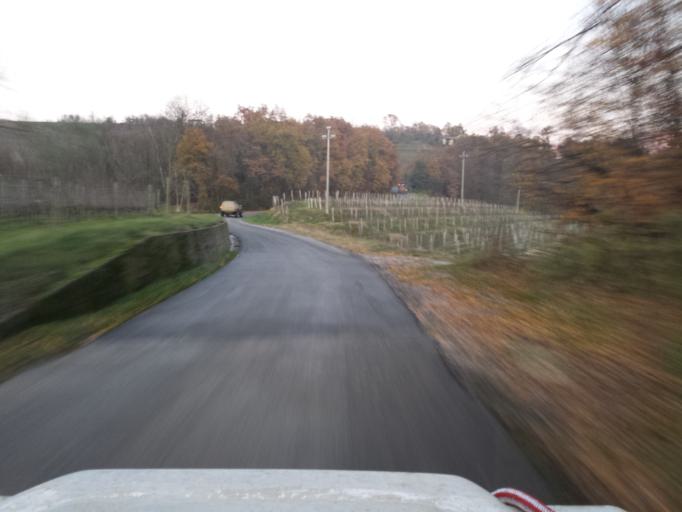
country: IT
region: Friuli Venezia Giulia
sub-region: Provincia di Udine
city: Corno di Rosazzo
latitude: 45.9889
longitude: 13.4743
